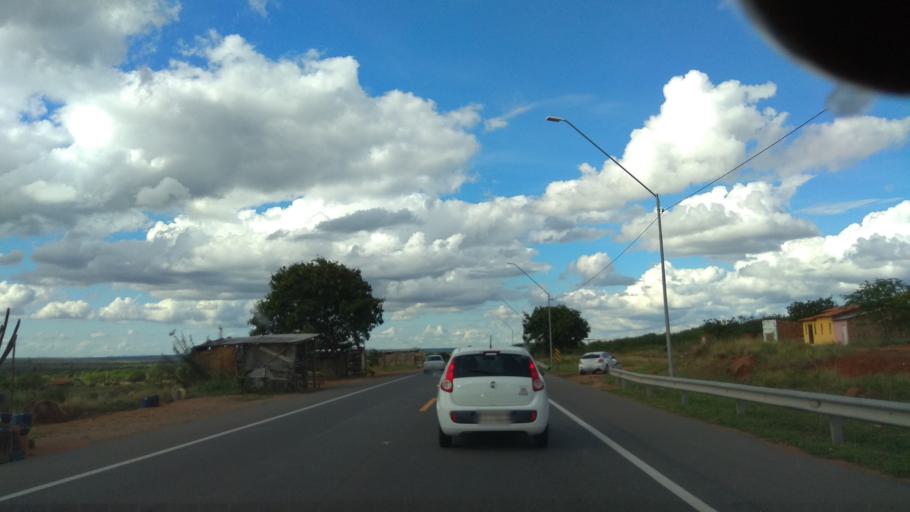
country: BR
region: Bahia
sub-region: Castro Alves
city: Castro Alves
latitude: -12.6236
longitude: -39.5902
